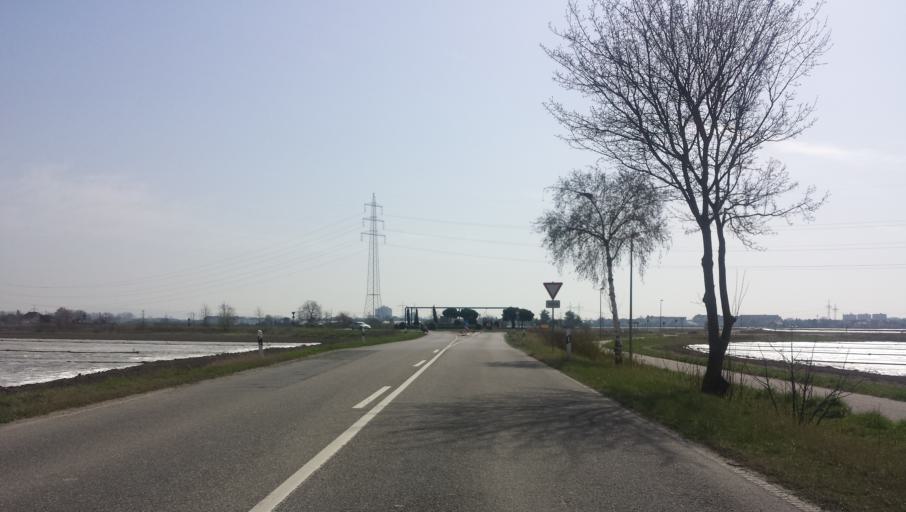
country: DE
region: Rheinland-Pfalz
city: Mutterstadt
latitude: 49.4328
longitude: 8.3670
